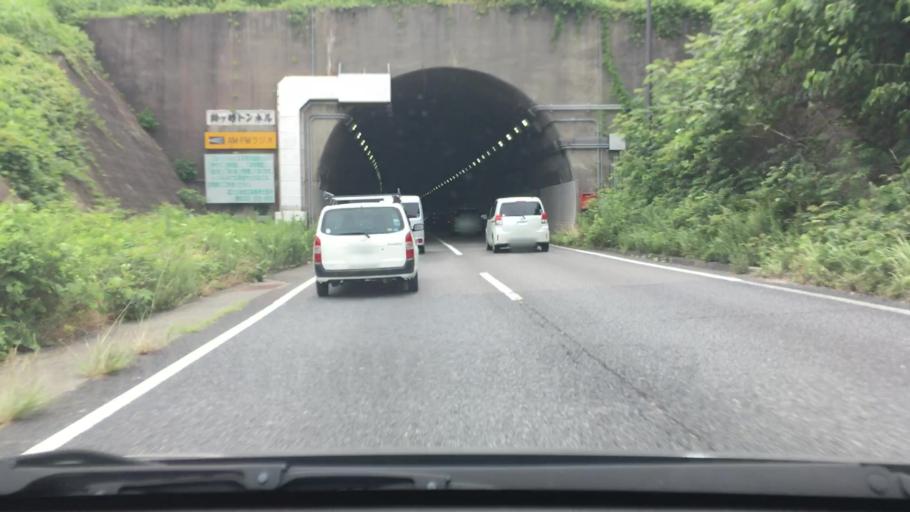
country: JP
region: Hiroshima
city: Hiroshima-shi
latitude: 34.3847
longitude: 132.3943
